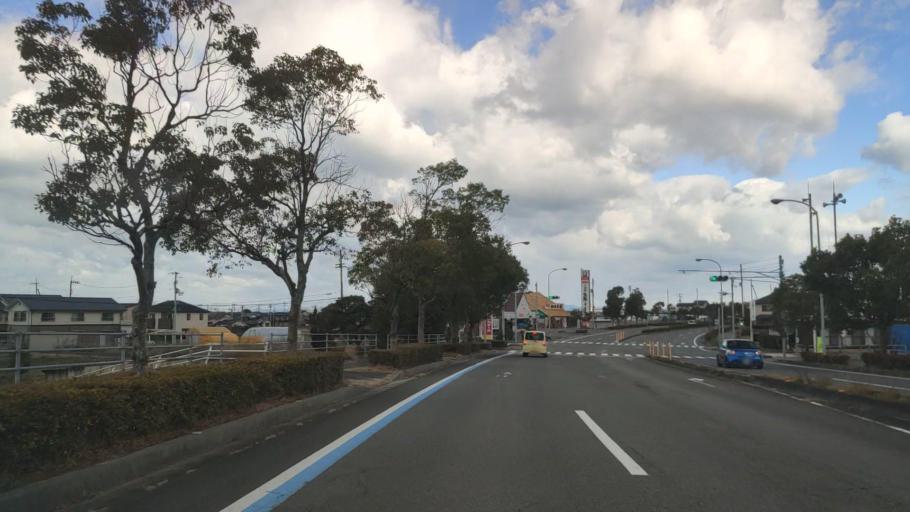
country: JP
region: Ehime
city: Hojo
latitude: 33.9484
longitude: 132.7744
